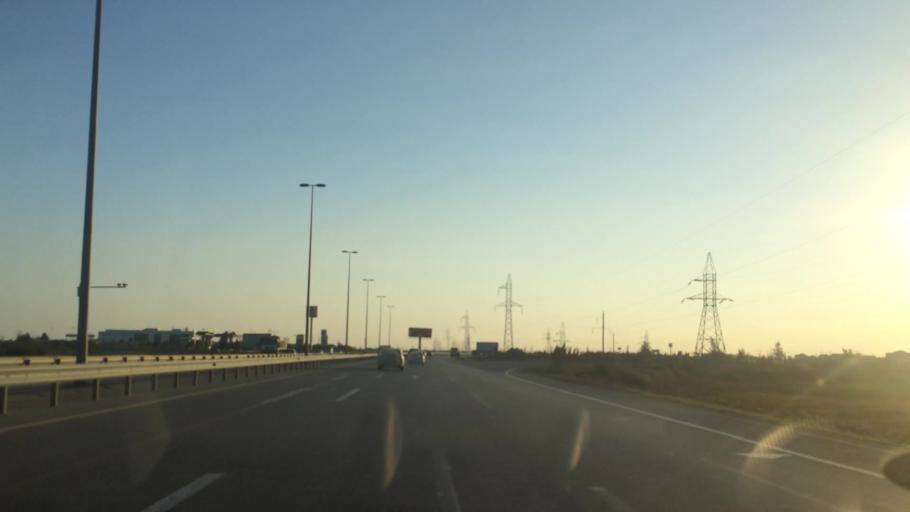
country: AZ
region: Baki
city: Qobustan
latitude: 39.9728
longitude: 49.4168
